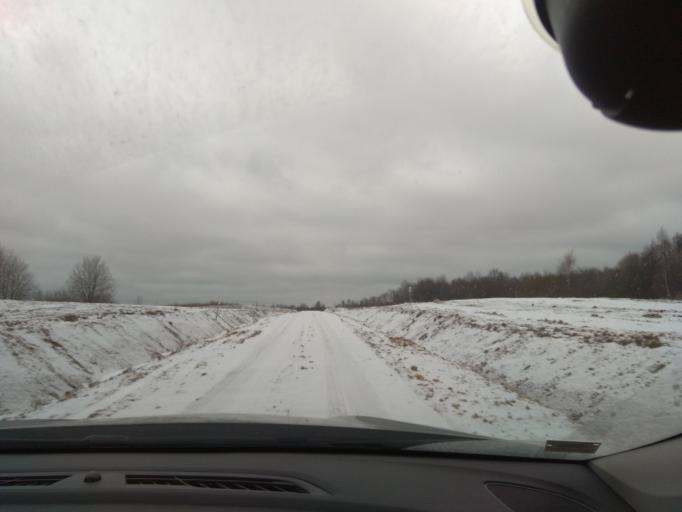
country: LT
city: Lentvaris
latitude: 54.6482
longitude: 25.0830
